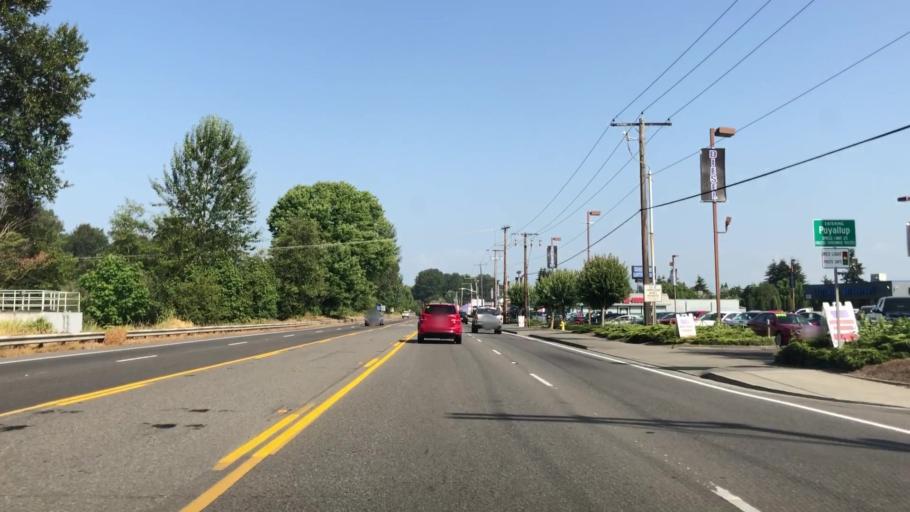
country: US
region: Washington
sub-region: Pierce County
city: Puyallup
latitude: 47.2067
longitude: -122.3215
